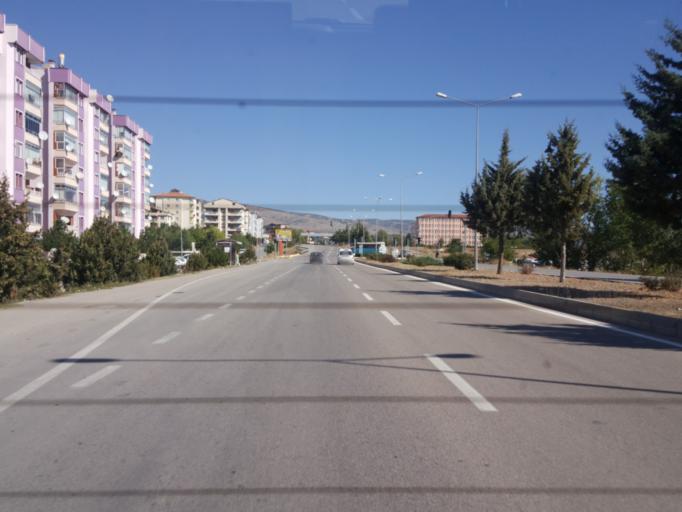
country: TR
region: Tokat
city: Zile
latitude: 40.3039
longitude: 35.8986
